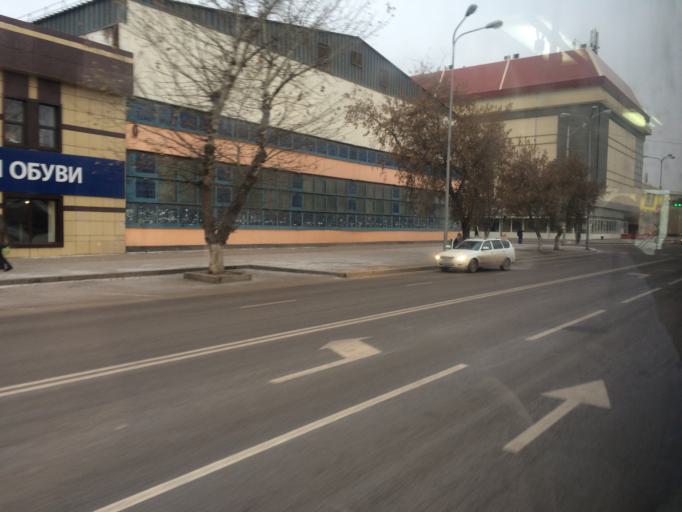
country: KZ
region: Astana Qalasy
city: Astana
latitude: 51.1723
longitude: 71.4384
